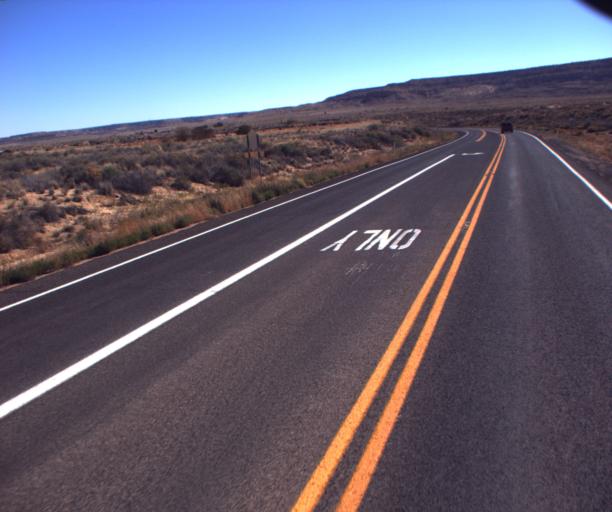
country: US
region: Arizona
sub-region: Navajo County
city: First Mesa
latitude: 35.8753
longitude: -110.6063
